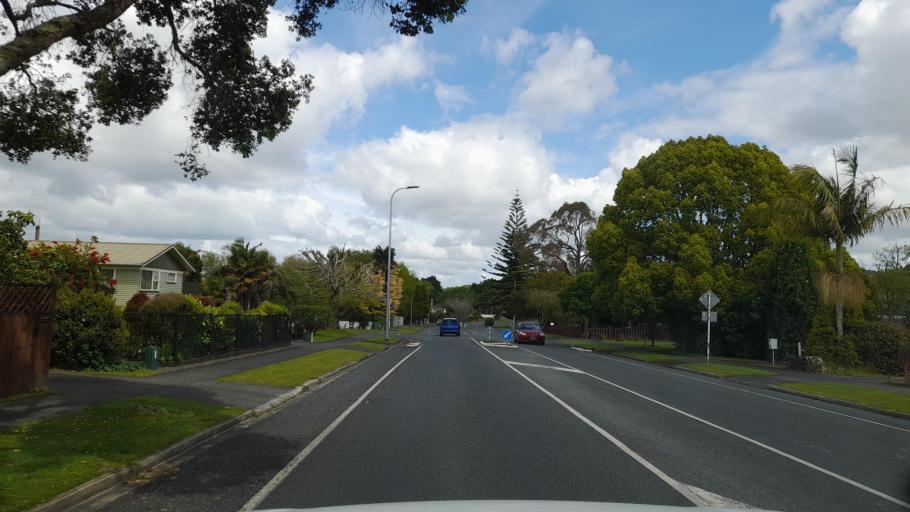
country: NZ
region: Northland
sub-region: Whangarei
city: Whangarei
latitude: -35.6953
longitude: 174.3046
